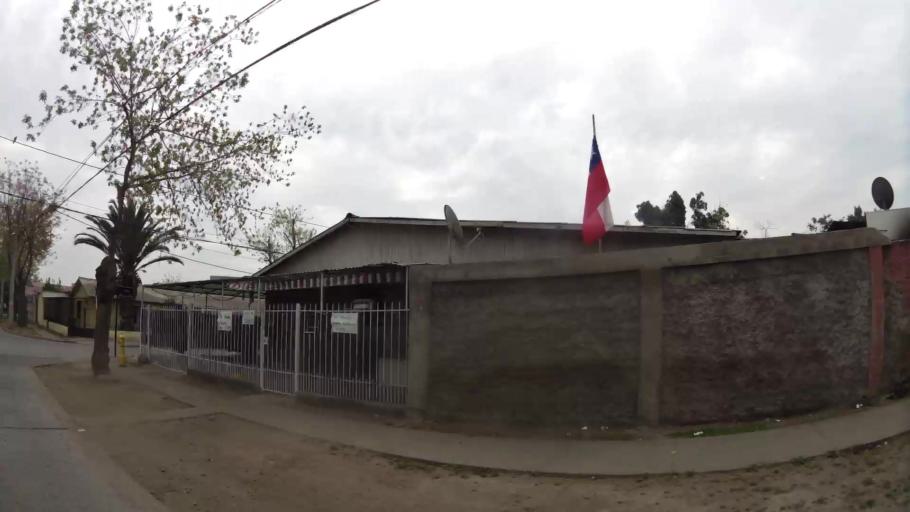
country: CL
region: Santiago Metropolitan
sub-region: Provincia de Santiago
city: Villa Presidente Frei, Nunoa, Santiago, Chile
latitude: -33.4711
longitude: -70.5938
